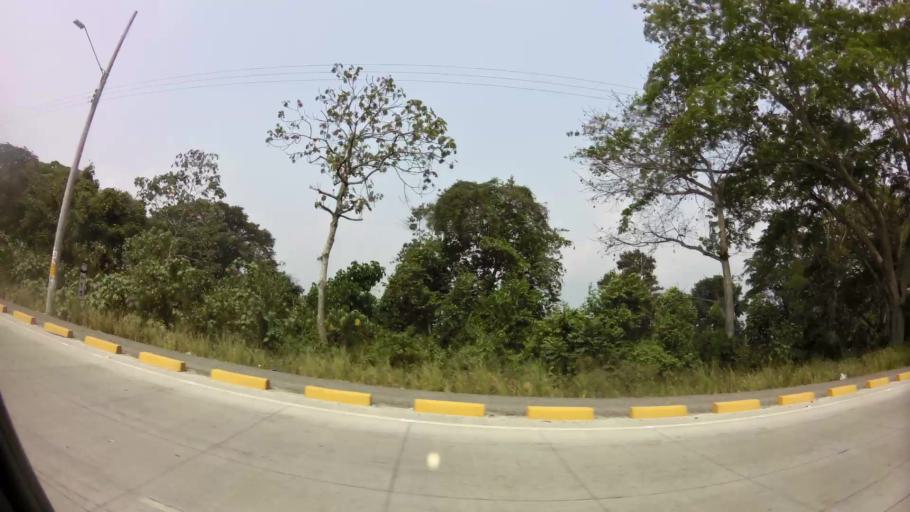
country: HN
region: Cortes
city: San Pedro Sula
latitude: 15.5292
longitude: -88.0058
